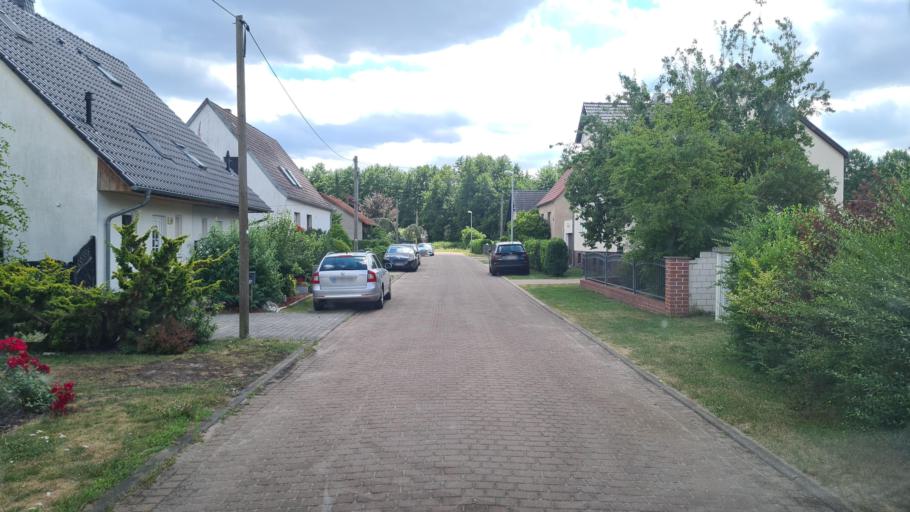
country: DE
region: Brandenburg
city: Luckenwalde
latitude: 52.1098
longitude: 13.2052
